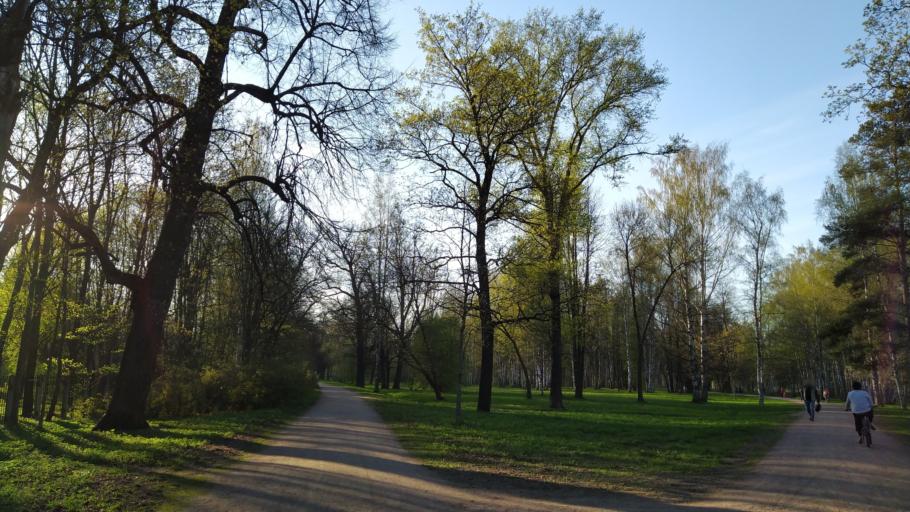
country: RU
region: St.-Petersburg
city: Pavlovsk
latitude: 59.6979
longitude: 30.4287
